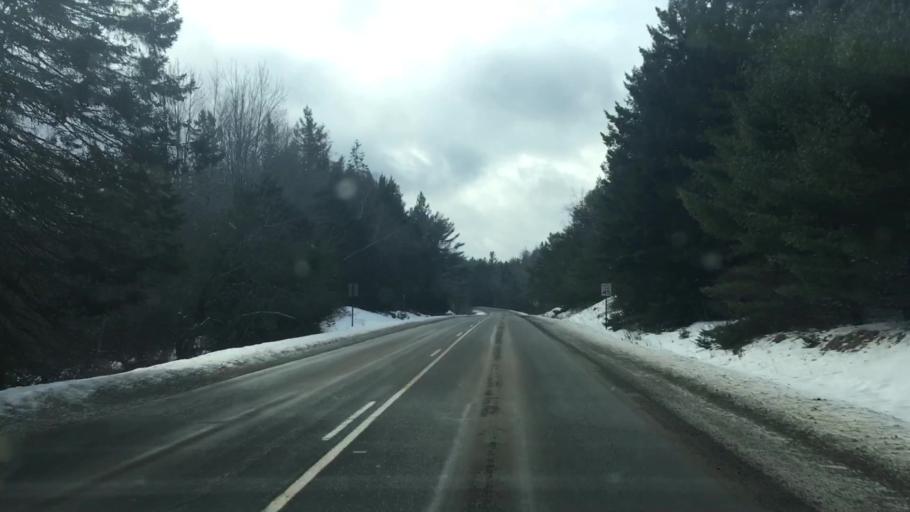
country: US
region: Maine
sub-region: Washington County
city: Calais
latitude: 45.0487
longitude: -67.3267
